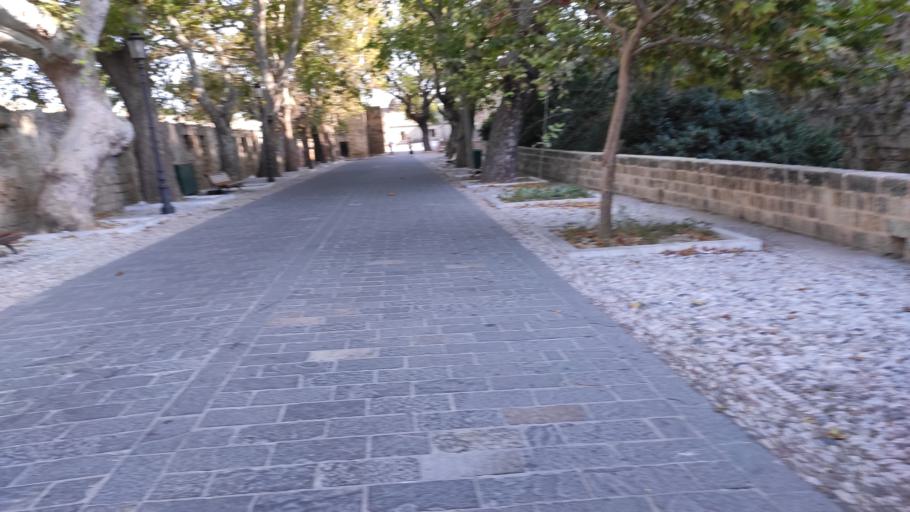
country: GR
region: South Aegean
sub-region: Nomos Dodekanisou
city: Rodos
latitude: 36.4454
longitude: 28.2233
